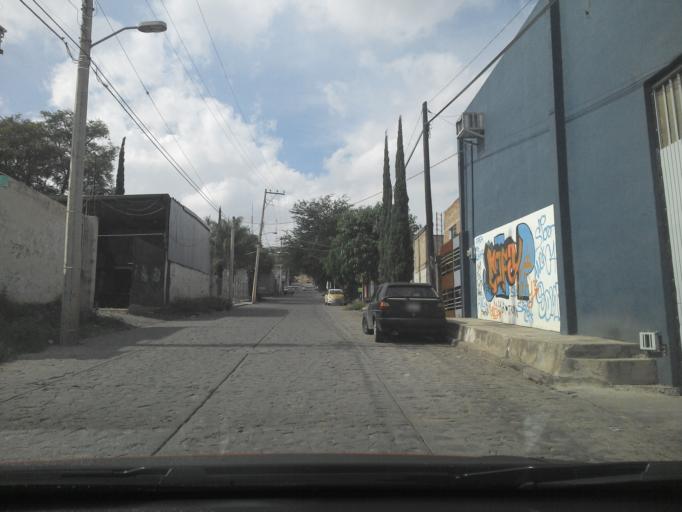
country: MX
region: Jalisco
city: Las Pintas de Arriba
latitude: 20.5944
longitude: -103.3493
